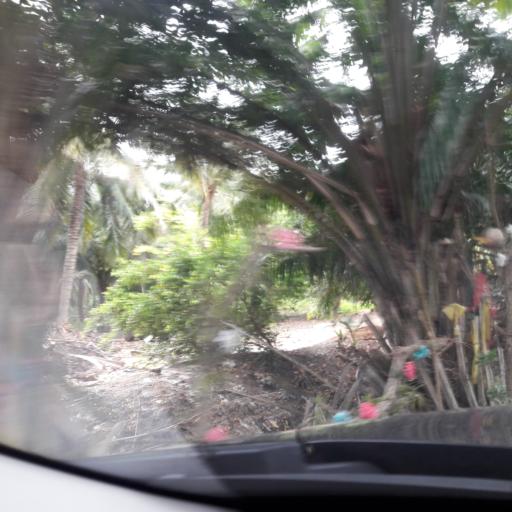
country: TH
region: Ratchaburi
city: Damnoen Saduak
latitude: 13.5764
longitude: 99.9392
